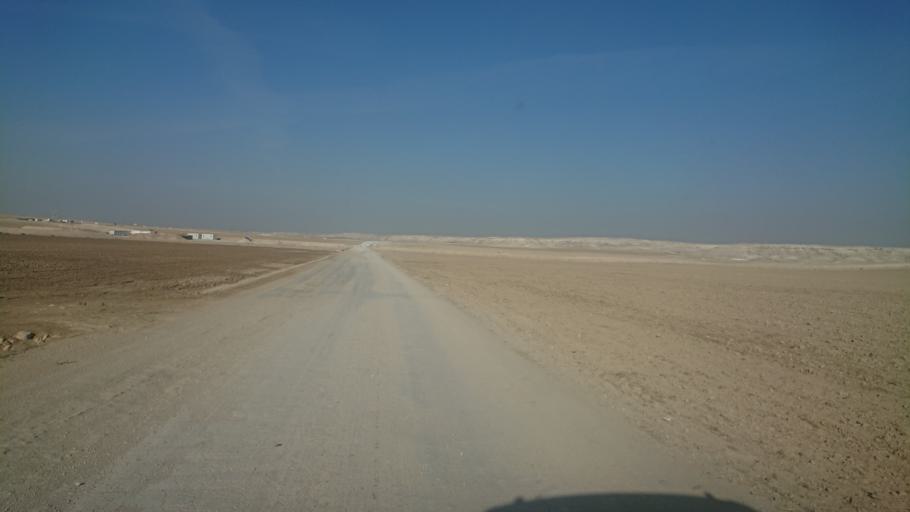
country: TR
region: Aksaray
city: Sultanhani
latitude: 38.0652
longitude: 33.6156
